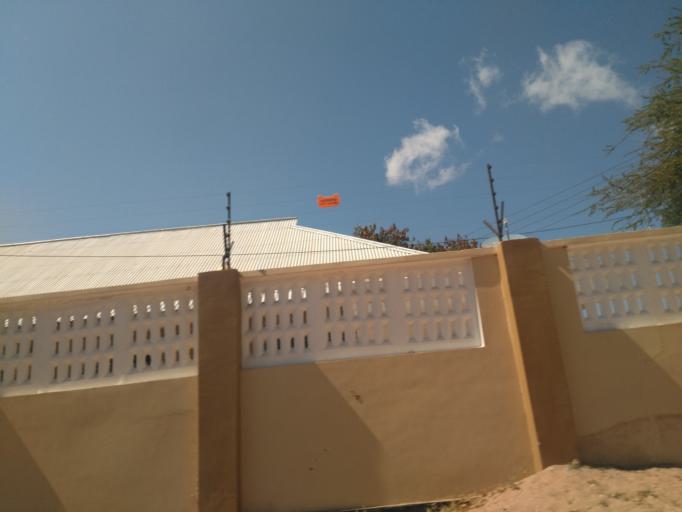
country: TZ
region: Dodoma
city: Dodoma
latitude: -6.1600
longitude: 35.7561
